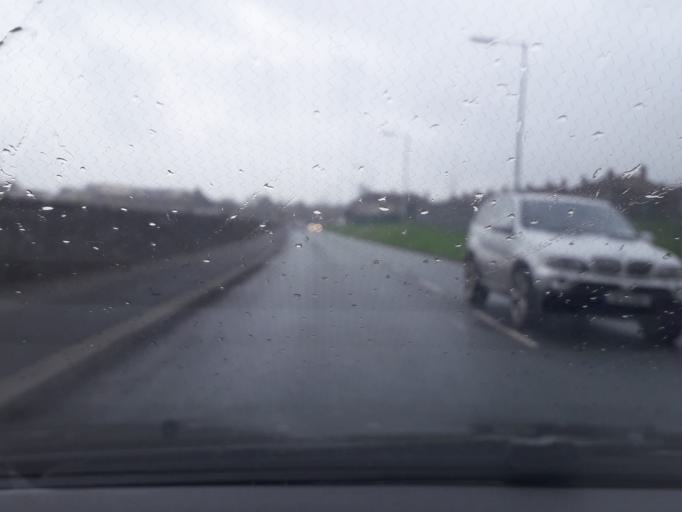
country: IE
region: Leinster
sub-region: Fingal County
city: Swords
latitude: 53.4672
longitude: -6.2193
